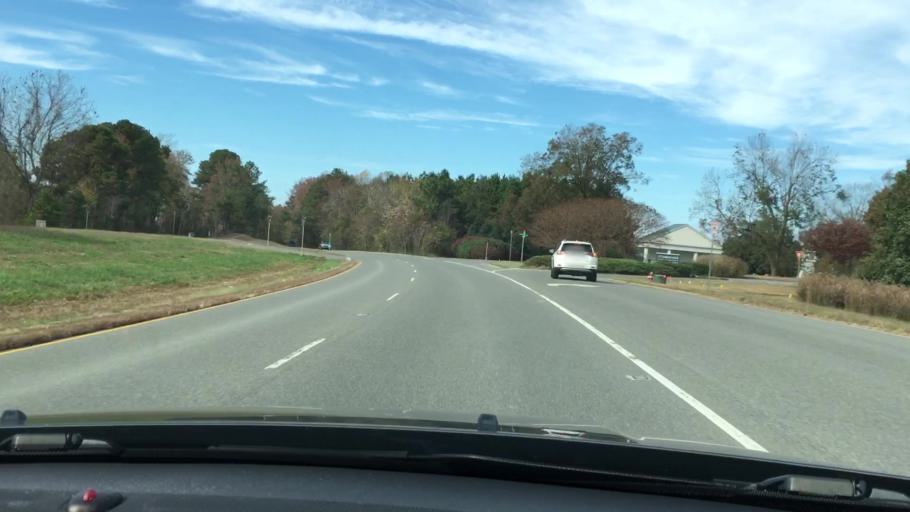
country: US
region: Virginia
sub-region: King William County
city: West Point
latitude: 37.4089
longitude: -76.8101
